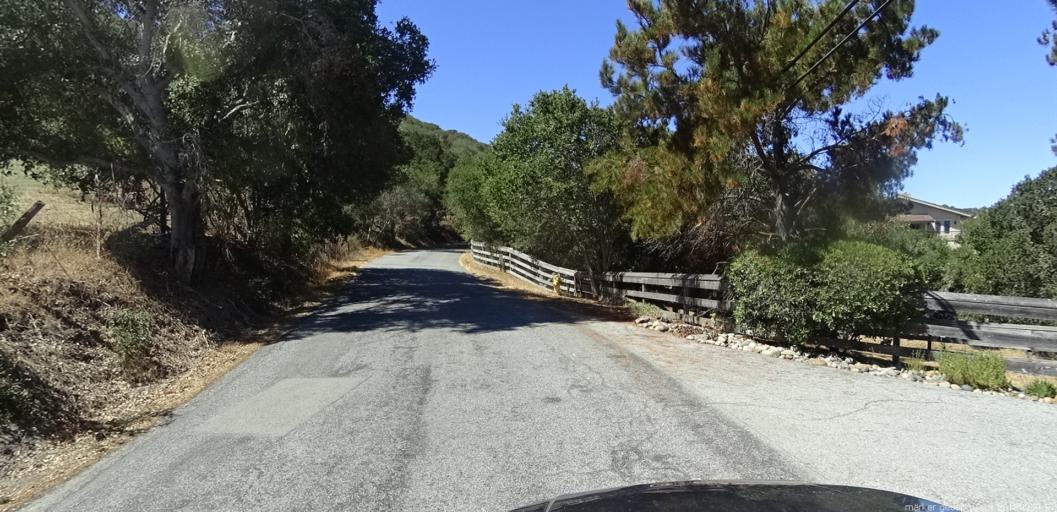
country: US
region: California
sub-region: Monterey County
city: Carmel Valley Village
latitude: 36.5515
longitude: -121.7393
